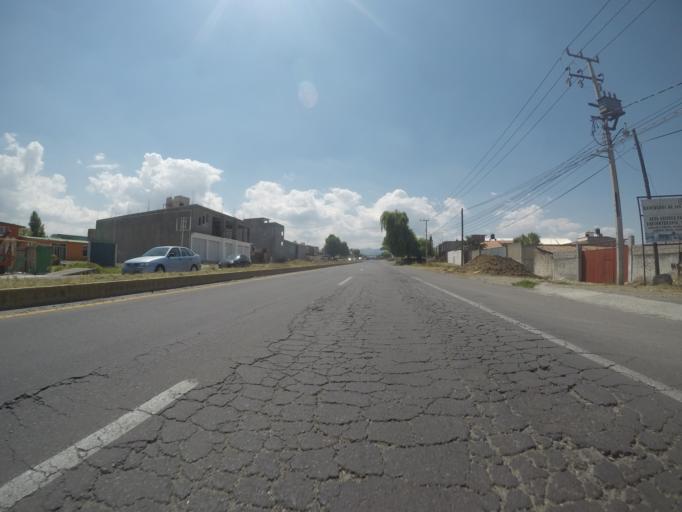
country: MX
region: Mexico
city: San Juan de las Huertas
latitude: 19.2512
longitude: -99.7536
